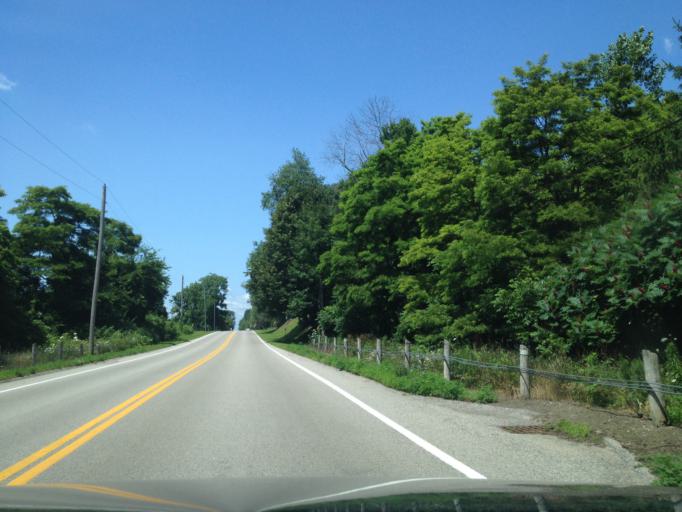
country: CA
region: Ontario
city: Aylmer
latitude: 42.6206
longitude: -80.7153
